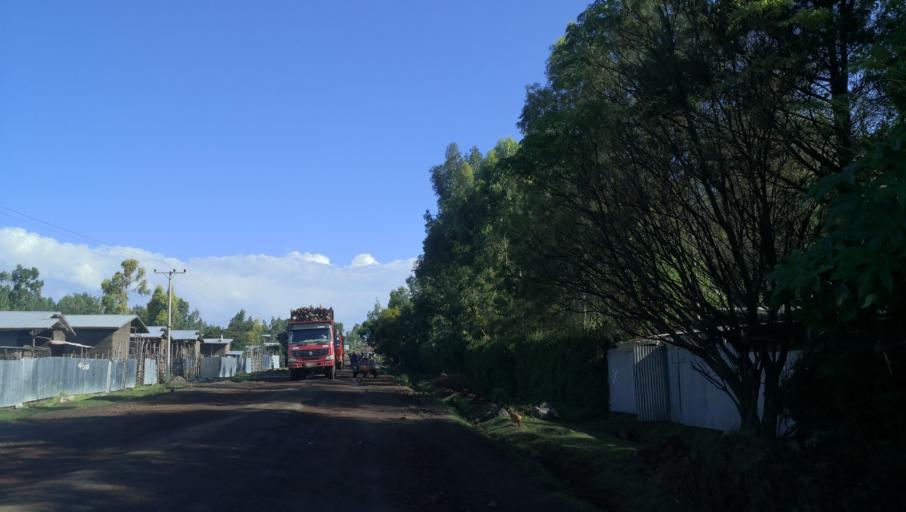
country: ET
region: Oromiya
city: Tulu Bolo
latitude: 8.6527
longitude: 38.2190
